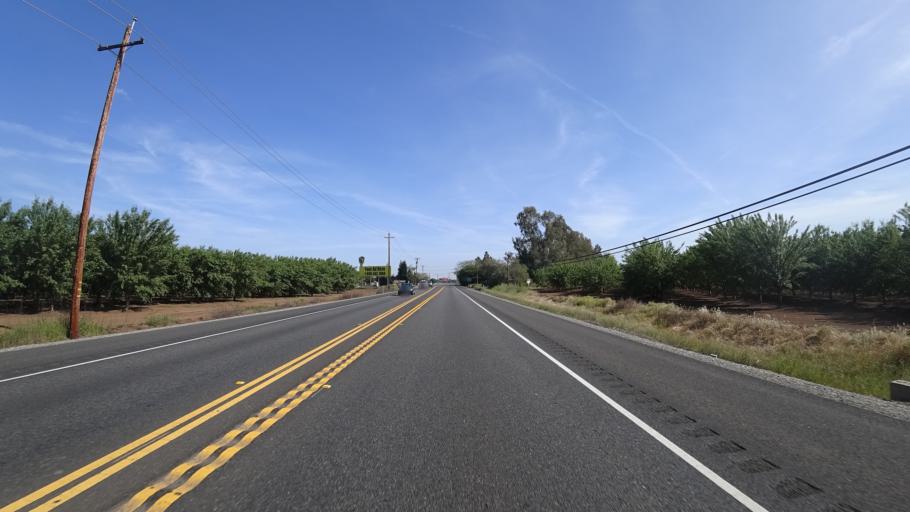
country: US
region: California
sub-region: Butte County
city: Chico
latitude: 39.7998
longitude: -121.9048
